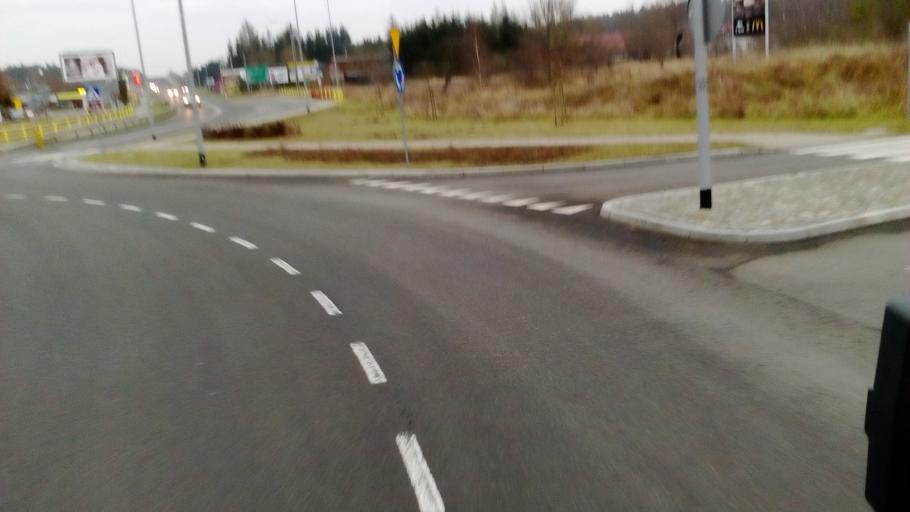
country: PL
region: West Pomeranian Voivodeship
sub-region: Powiat policki
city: Dobra
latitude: 53.4531
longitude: 14.3765
